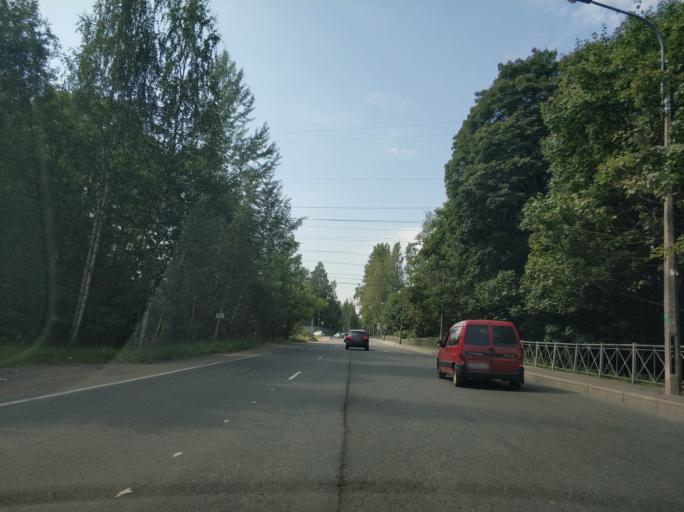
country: RU
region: St.-Petersburg
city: Krasnogvargeisky
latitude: 59.9785
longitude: 30.5012
